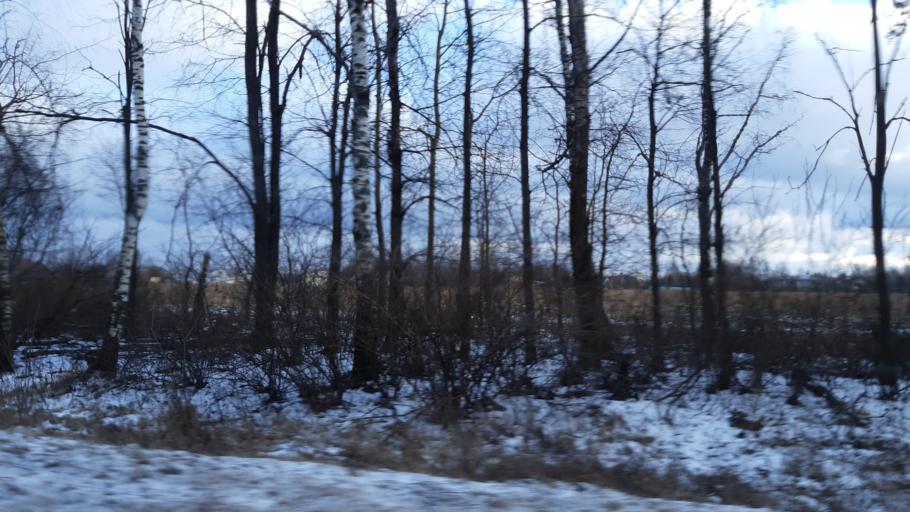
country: RU
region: Moskovskaya
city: Noginsk-9
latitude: 56.0080
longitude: 38.5585
